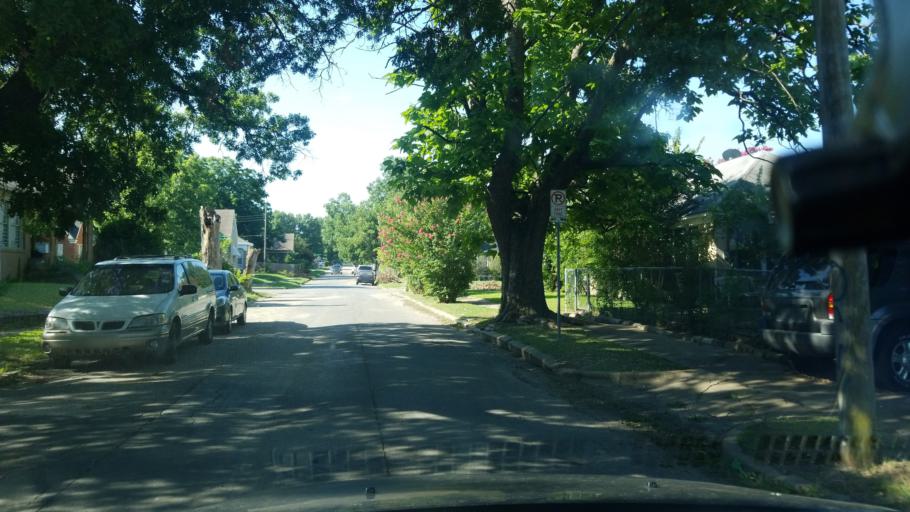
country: US
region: Texas
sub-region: Dallas County
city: Dallas
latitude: 32.7228
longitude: -96.8246
